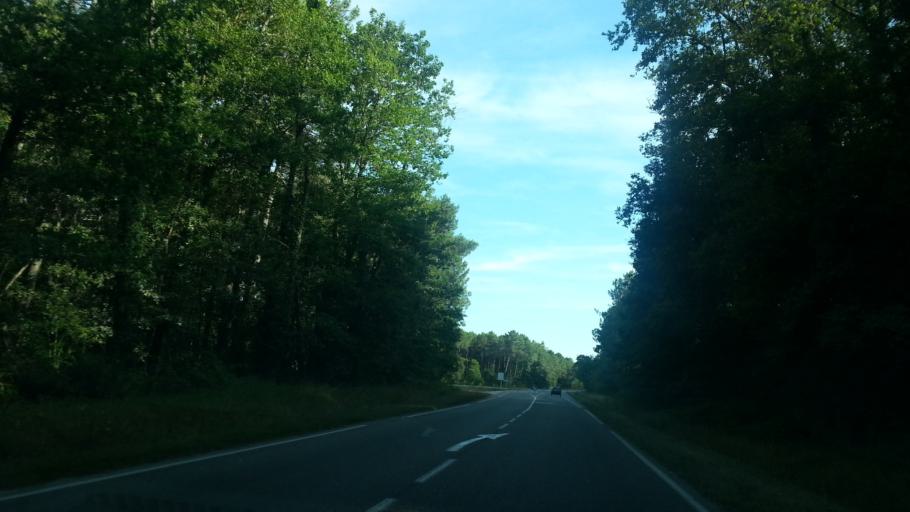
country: FR
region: Aquitaine
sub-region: Departement de la Gironde
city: Illats
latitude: 44.6142
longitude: -0.3724
